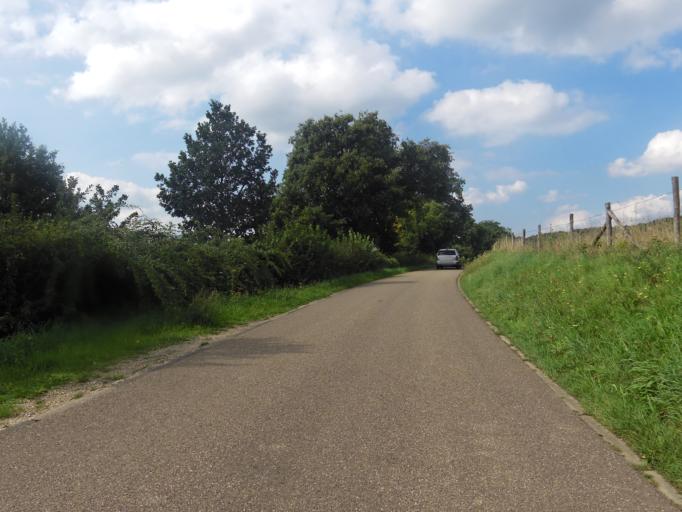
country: NL
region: Limburg
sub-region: Gemeente Schinnen
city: Puth
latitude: 50.9442
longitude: 5.8684
